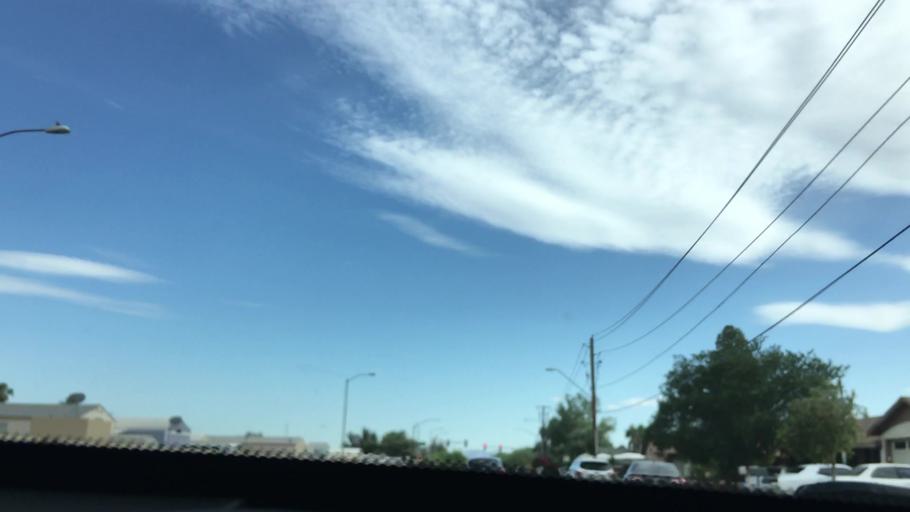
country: US
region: Arizona
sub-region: Maricopa County
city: Peoria
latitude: 33.5828
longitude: -112.2290
